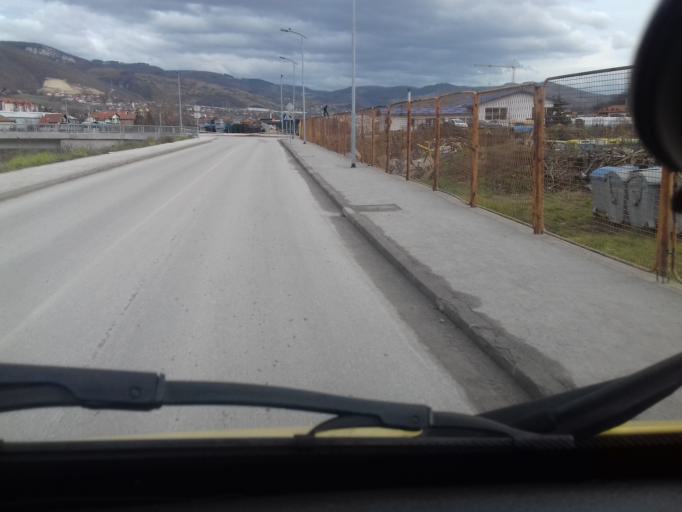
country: BA
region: Federation of Bosnia and Herzegovina
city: Zenica
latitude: 44.1906
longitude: 17.9326
